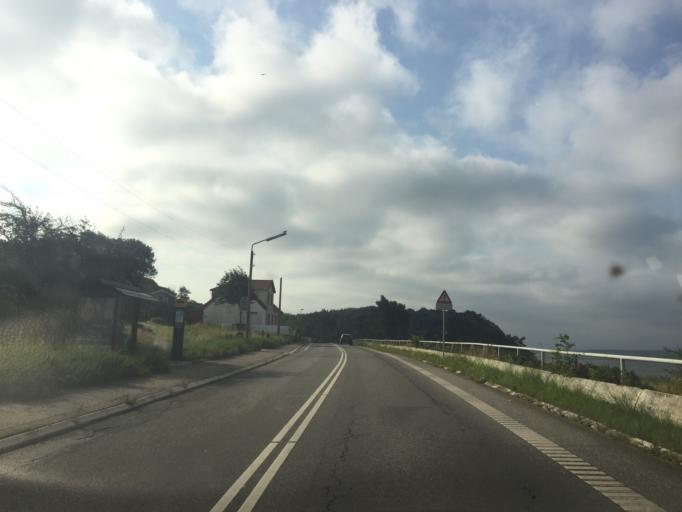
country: DK
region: Capital Region
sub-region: Halsnaes Kommune
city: Frederiksvaerk
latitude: 55.9573
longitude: 12.0205
